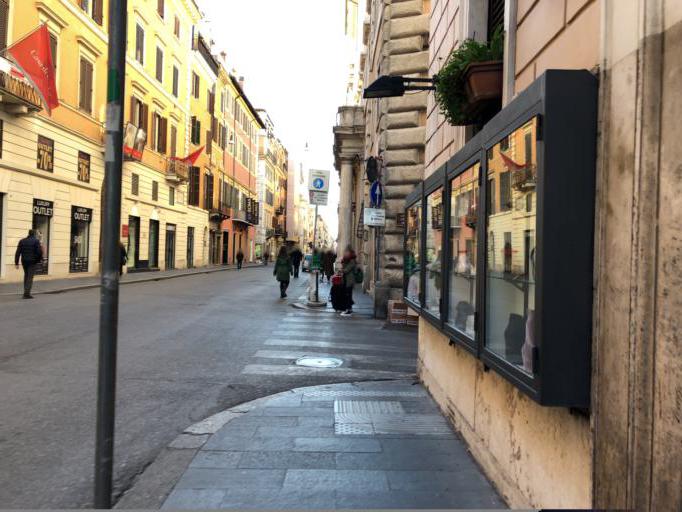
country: VA
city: Vatican City
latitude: 41.9092
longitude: 12.4769
